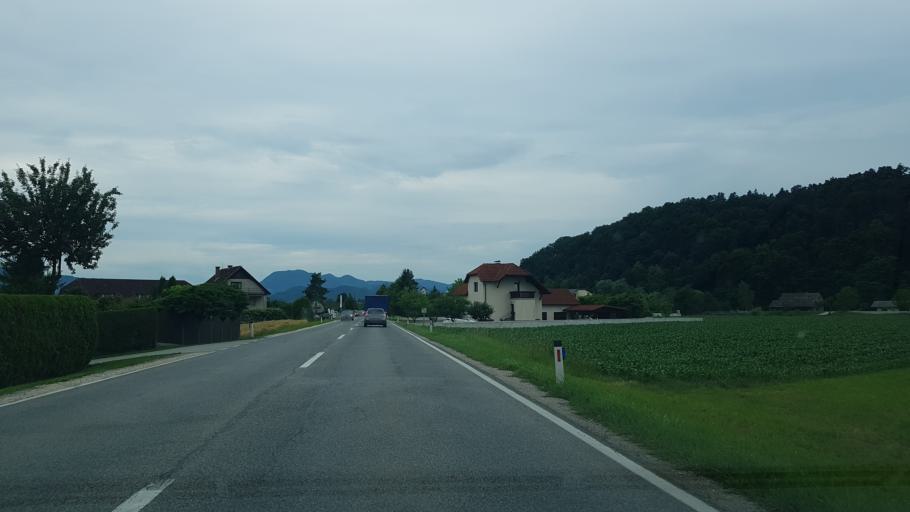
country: SI
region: Celje
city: Trnovlje pri Celju
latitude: 46.2750
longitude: 15.2968
